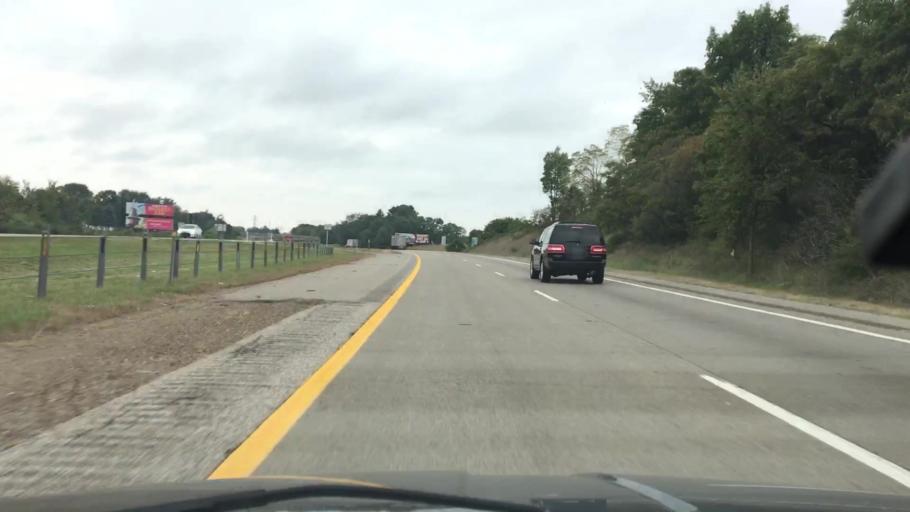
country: US
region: Michigan
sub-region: Berrien County
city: Coloma
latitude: 42.1740
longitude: -86.3141
